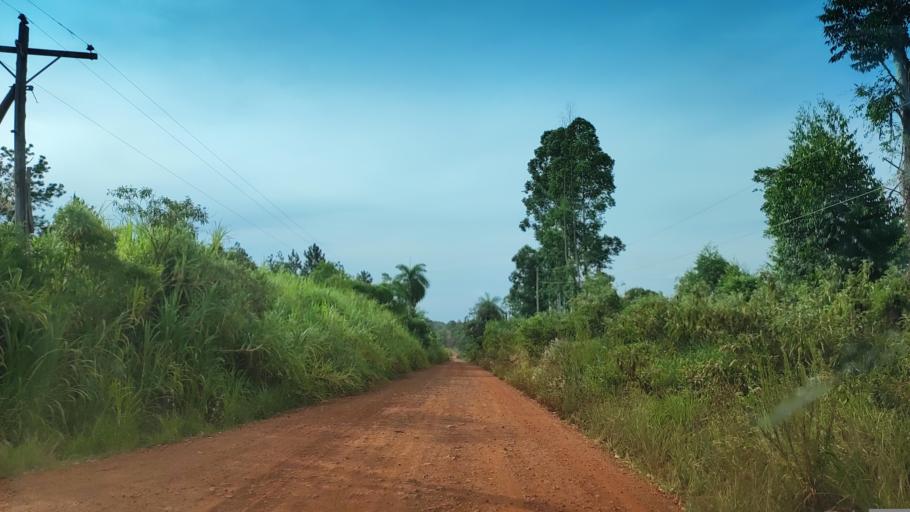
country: AR
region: Misiones
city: Gobernador Roca
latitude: -27.1852
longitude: -55.4923
